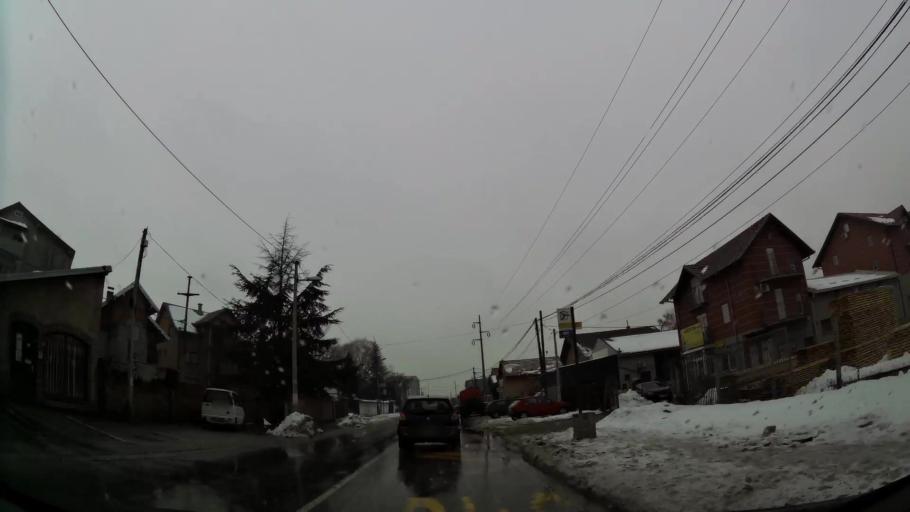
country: RS
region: Central Serbia
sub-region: Belgrade
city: Zemun
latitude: 44.8516
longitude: 20.3651
